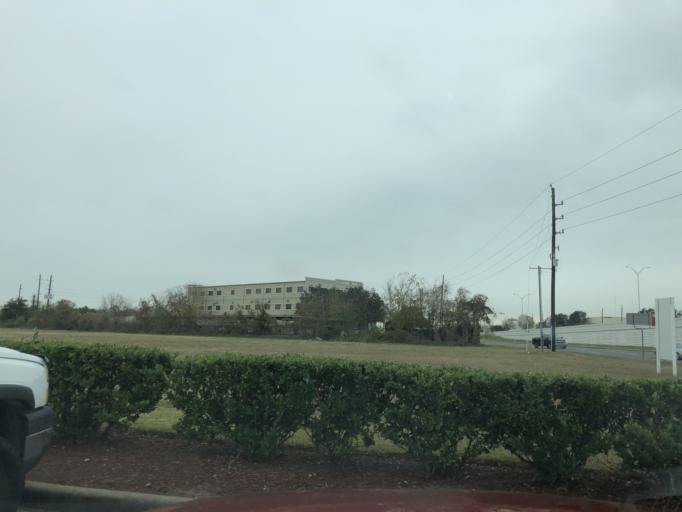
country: US
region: Texas
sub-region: Fort Bend County
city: Missouri City
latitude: 29.6442
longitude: -95.5380
